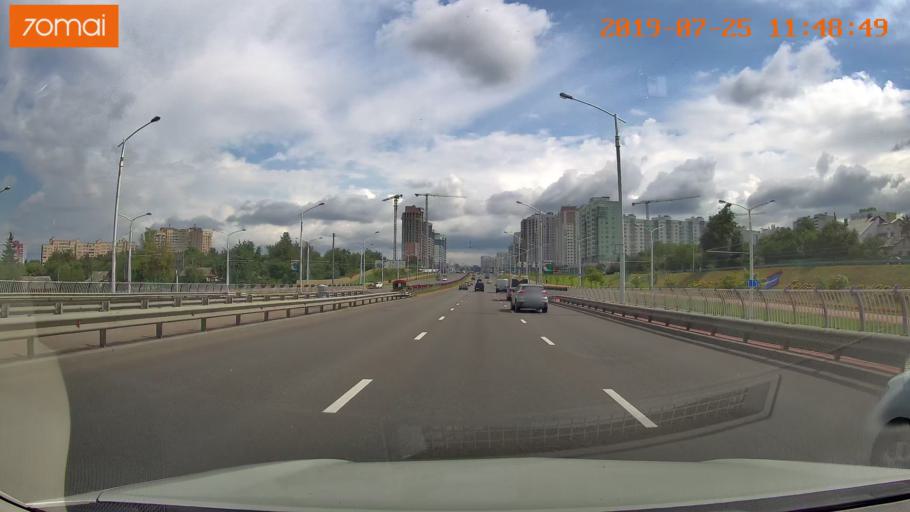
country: BY
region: Minsk
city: Syenitsa
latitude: 53.8840
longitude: 27.5087
